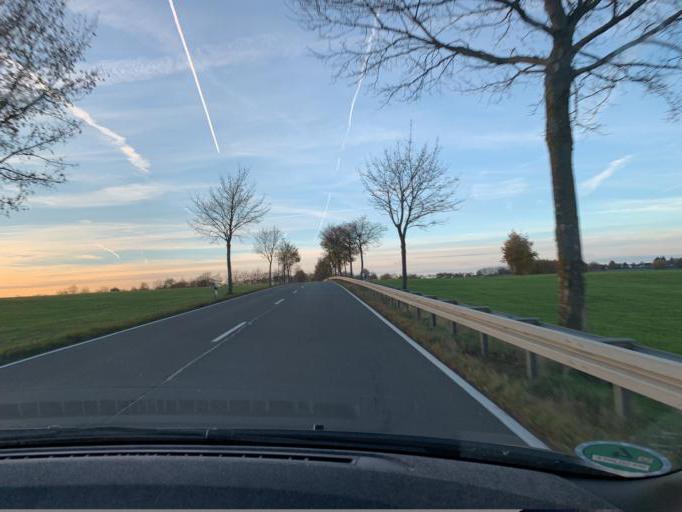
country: DE
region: North Rhine-Westphalia
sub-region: Regierungsbezirk Koln
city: Simmerath
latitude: 50.5958
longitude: 6.3508
